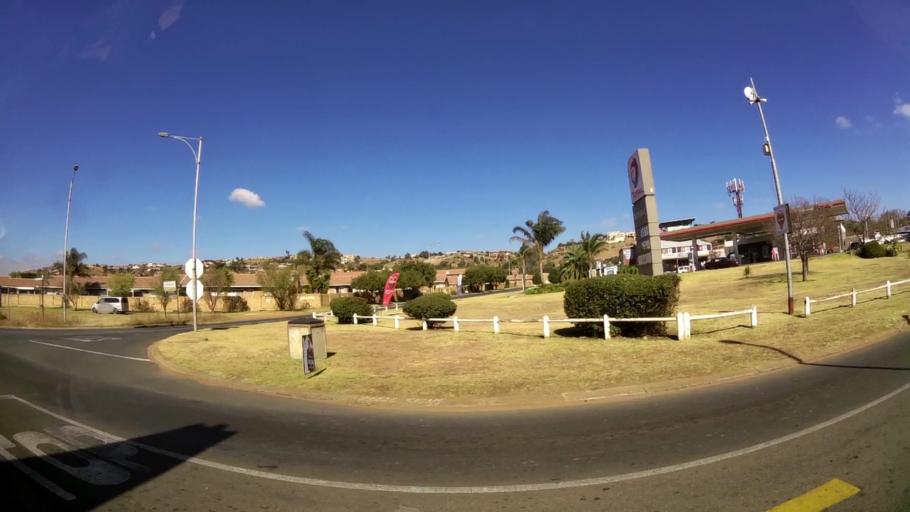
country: ZA
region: Gauteng
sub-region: West Rand District Municipality
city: Krugersdorp
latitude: -26.0898
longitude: 27.8203
